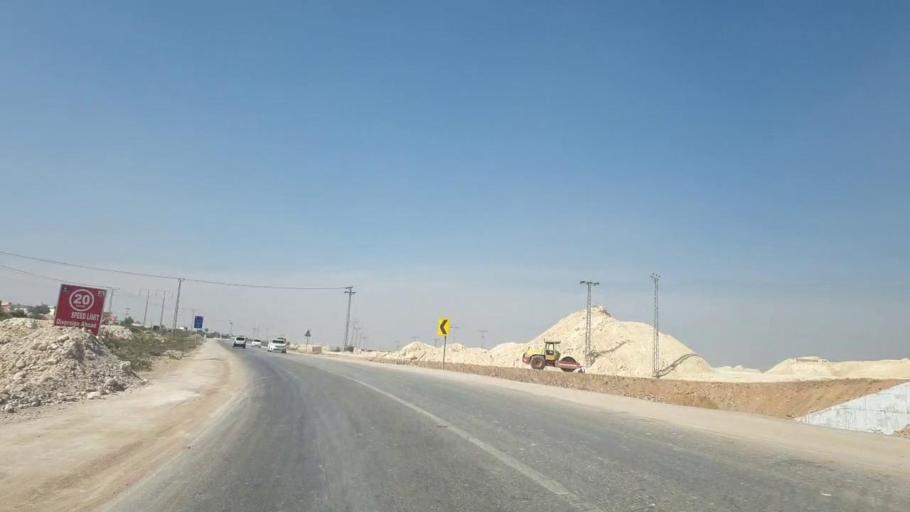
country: PK
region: Sindh
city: Hala
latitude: 25.7346
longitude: 68.2918
